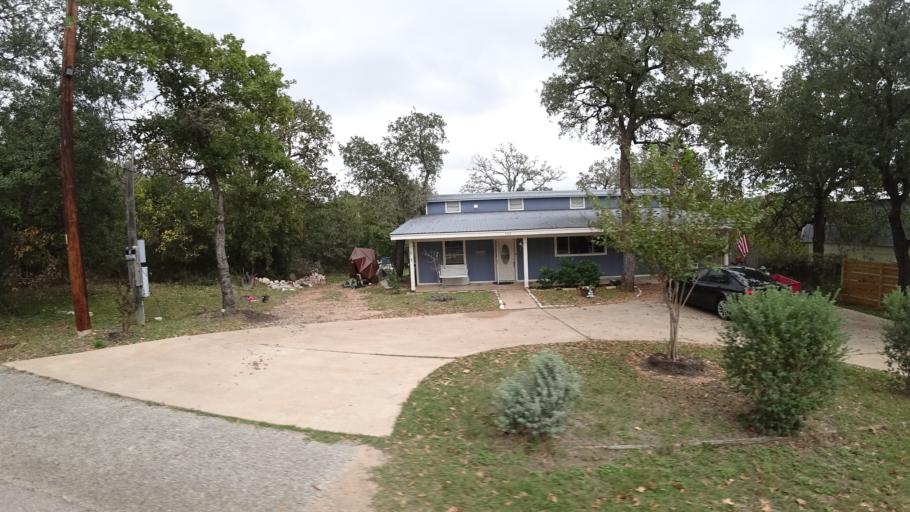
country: US
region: Texas
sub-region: Travis County
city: Bee Cave
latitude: 30.3324
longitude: -97.9284
